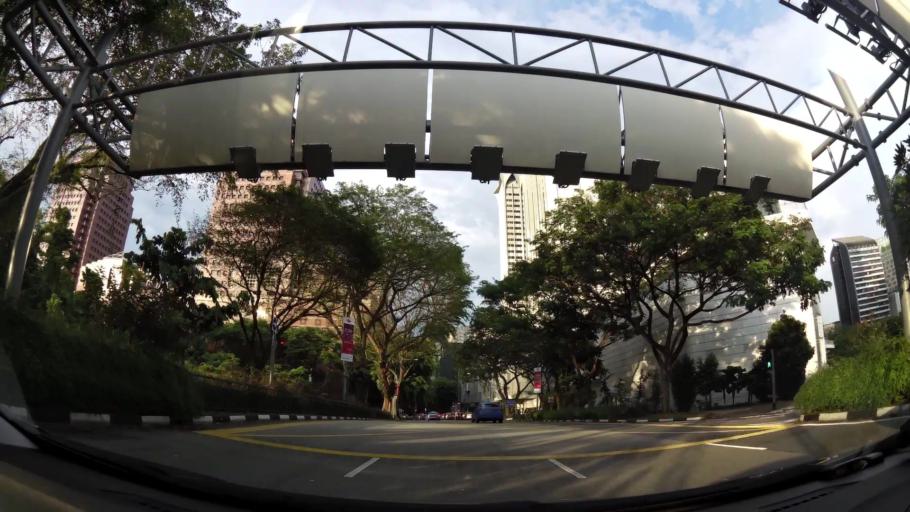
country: SG
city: Singapore
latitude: 1.3007
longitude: 103.8350
